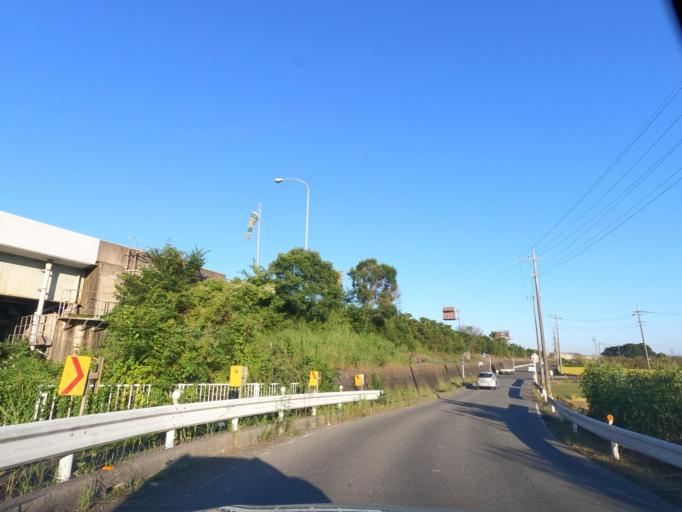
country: JP
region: Saitama
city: Kawagoe
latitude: 35.9099
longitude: 139.4447
